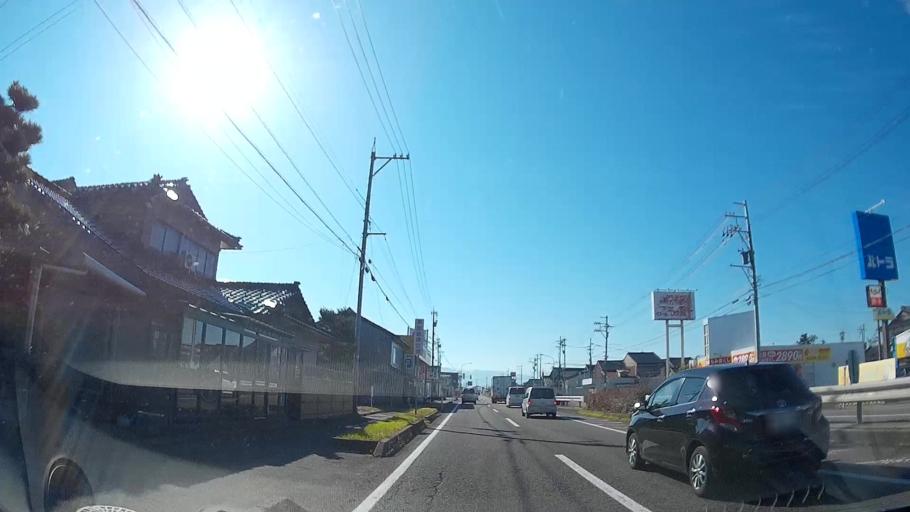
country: JP
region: Toyama
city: Takaoka
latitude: 36.6841
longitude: 136.9764
